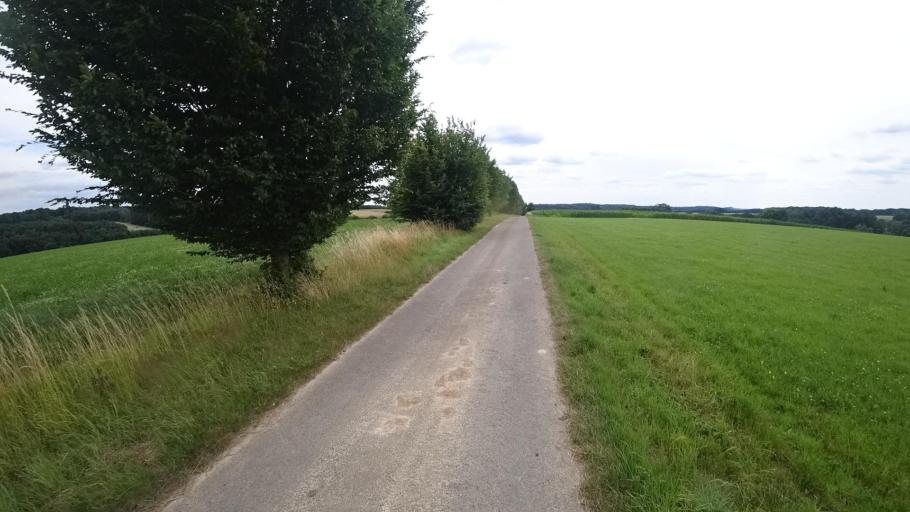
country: DE
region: Rheinland-Pfalz
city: Orfgen
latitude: 50.6703
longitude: 7.5377
